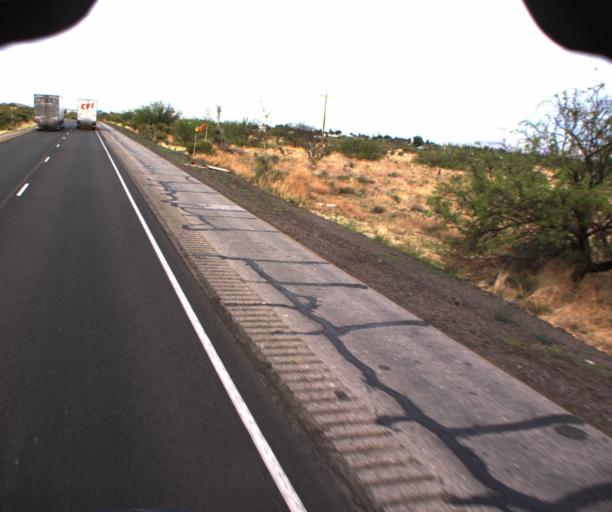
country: US
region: Arizona
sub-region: Cochise County
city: Mescal
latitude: 31.9632
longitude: -110.4216
